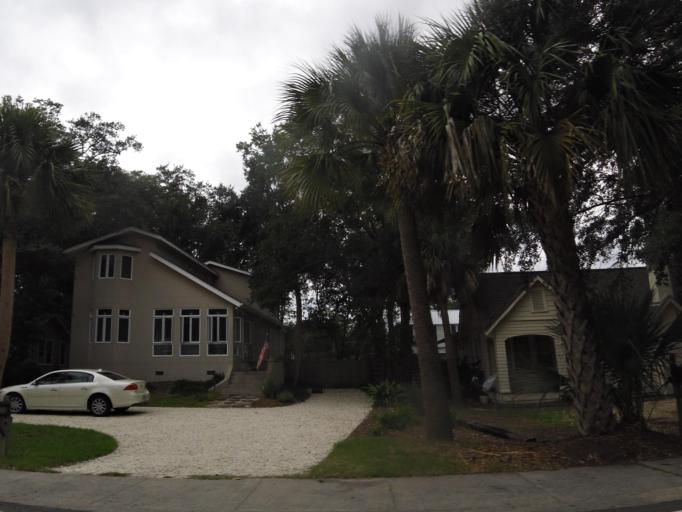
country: US
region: Georgia
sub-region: Glynn County
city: Saint Simons Island
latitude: 31.1395
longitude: -81.3826
